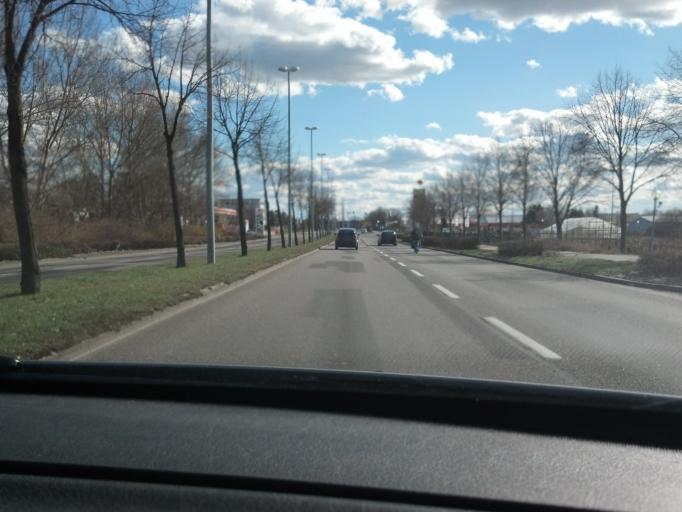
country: DE
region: Mecklenburg-Vorpommern
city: Neubrandenburg
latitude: 53.5847
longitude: 13.2717
